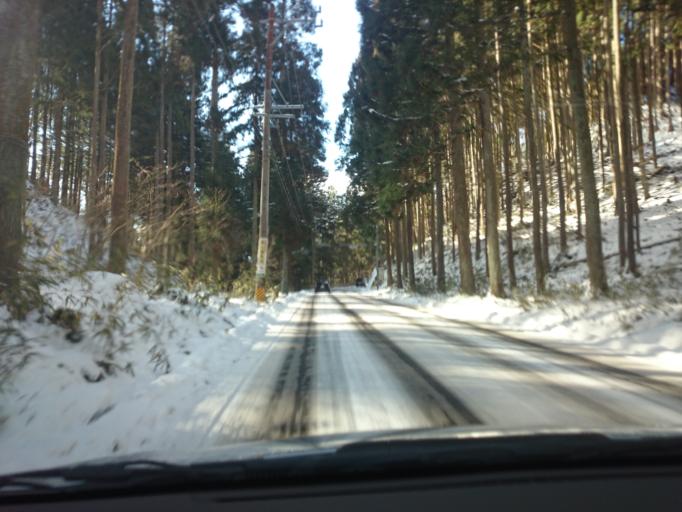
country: JP
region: Gifu
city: Gujo
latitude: 35.7354
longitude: 136.9889
